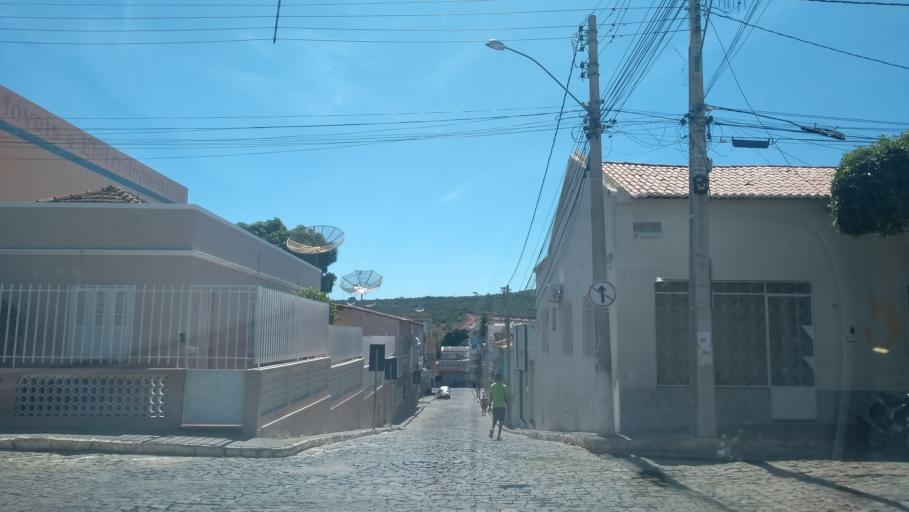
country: BR
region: Bahia
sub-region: Brumado
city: Brumado
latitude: -14.2053
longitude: -41.6667
